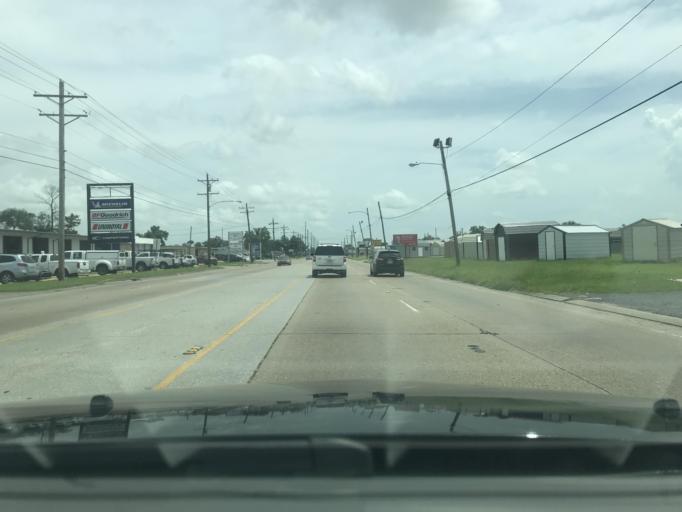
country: US
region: Louisiana
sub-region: Calcasieu Parish
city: Lake Charles
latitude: 30.2235
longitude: -93.1802
